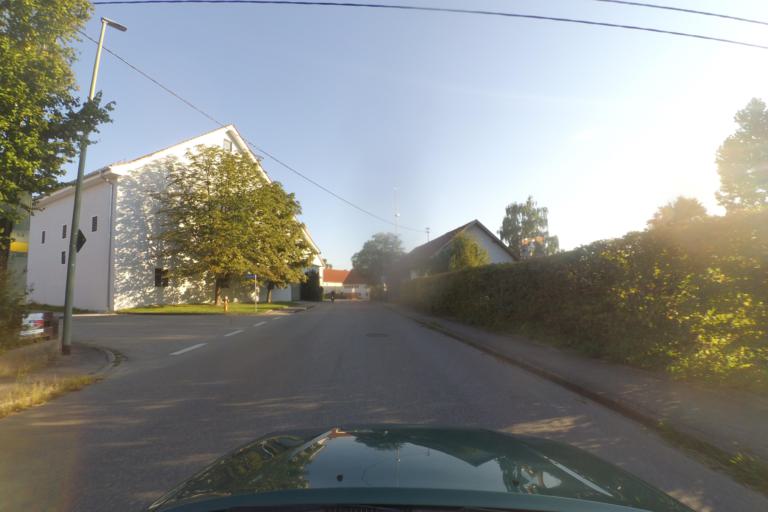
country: DE
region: Bavaria
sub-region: Upper Bavaria
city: Scheuring
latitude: 48.1708
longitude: 10.8965
